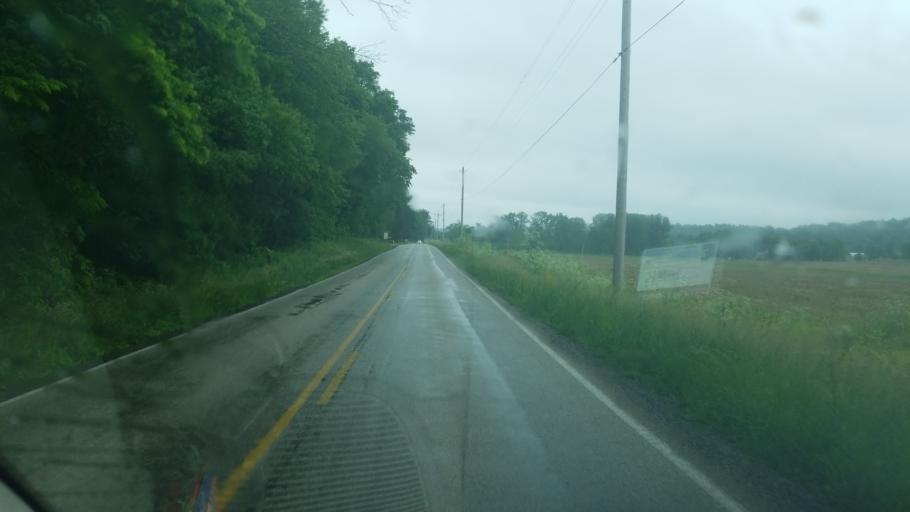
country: US
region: Ohio
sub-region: Sandusky County
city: Bellville
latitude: 40.6733
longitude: -82.4369
